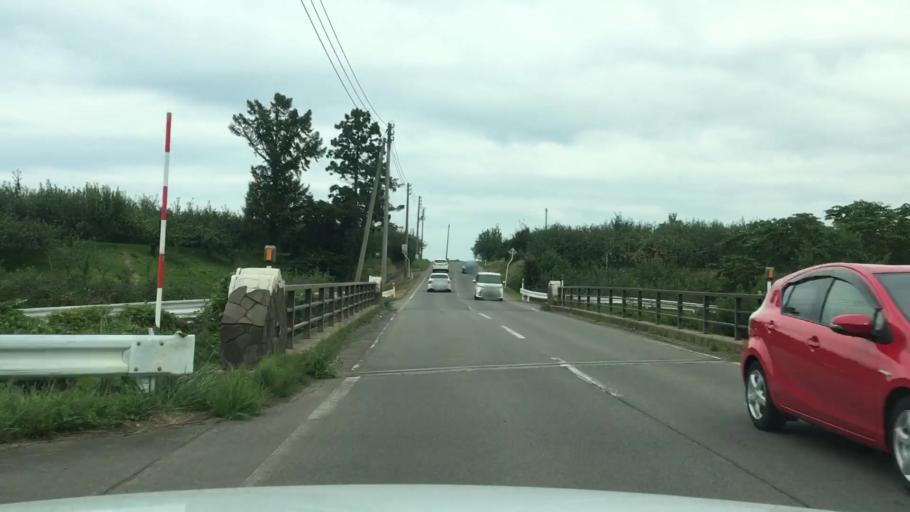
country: JP
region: Aomori
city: Hirosaki
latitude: 40.6557
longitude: 140.4206
